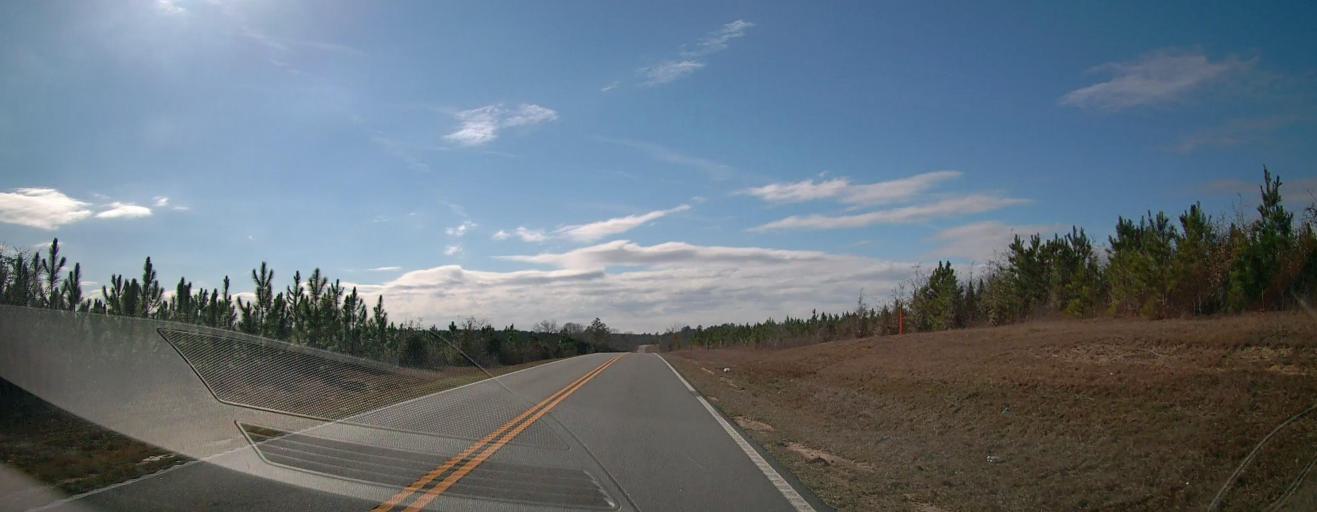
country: US
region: Georgia
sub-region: Taylor County
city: Butler
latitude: 32.4398
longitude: -84.2622
